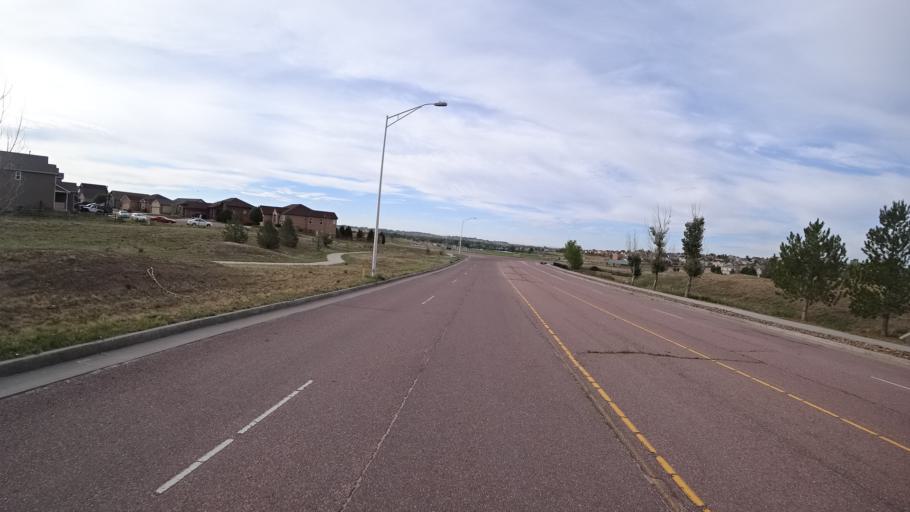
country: US
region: Colorado
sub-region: El Paso County
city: Fountain
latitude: 38.7163
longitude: -104.6862
